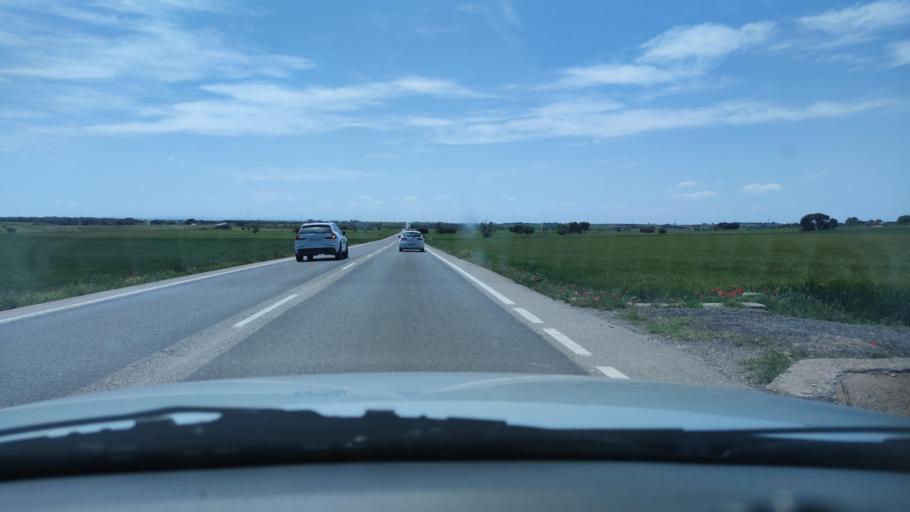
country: ES
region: Catalonia
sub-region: Provincia de Lleida
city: Mont-roig del Camp
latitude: 41.7399
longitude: 1.2203
